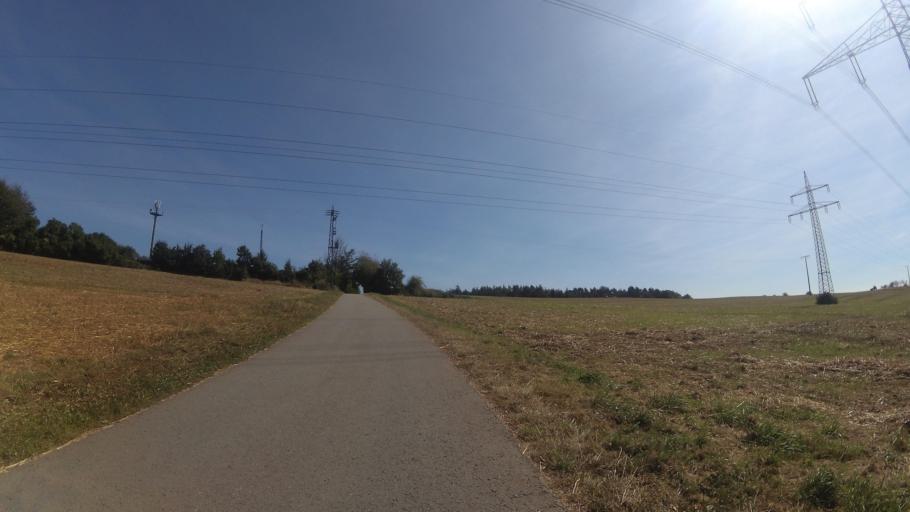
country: DE
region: Rheinland-Pfalz
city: Waldmohr
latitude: 49.4045
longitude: 7.3410
